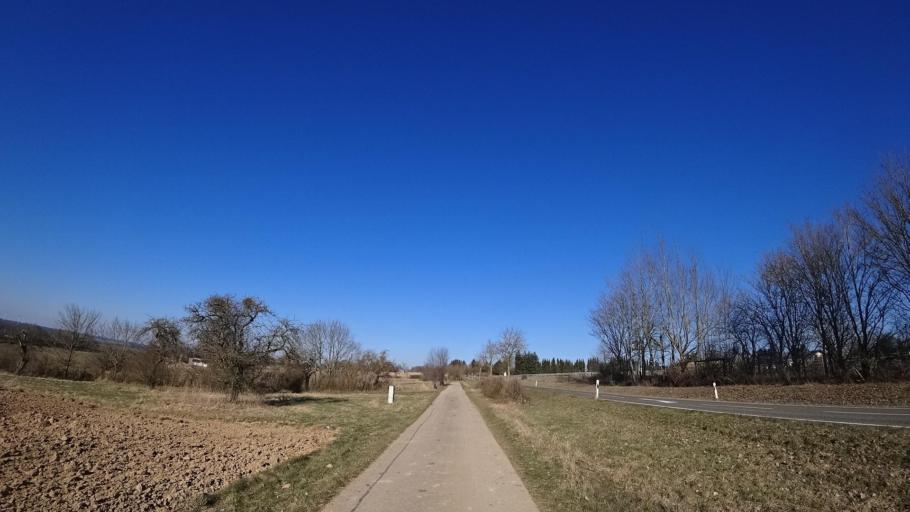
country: DE
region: Rheinland-Pfalz
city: Riesweiler
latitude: 49.9585
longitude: 7.5503
